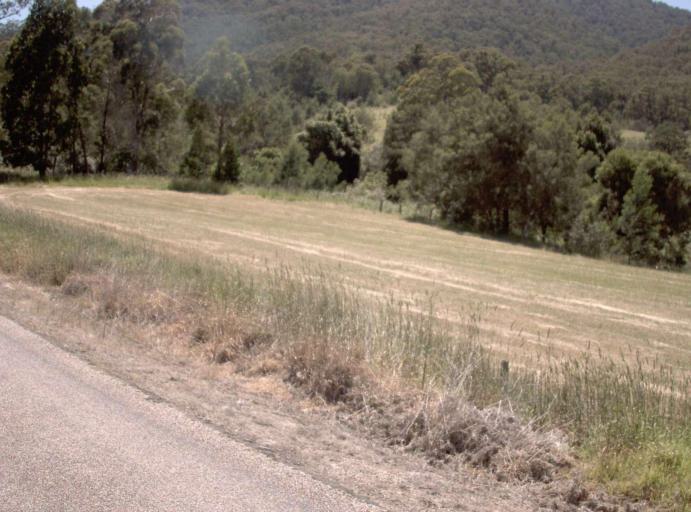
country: AU
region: Victoria
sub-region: East Gippsland
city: Lakes Entrance
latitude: -37.3925
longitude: 148.2182
